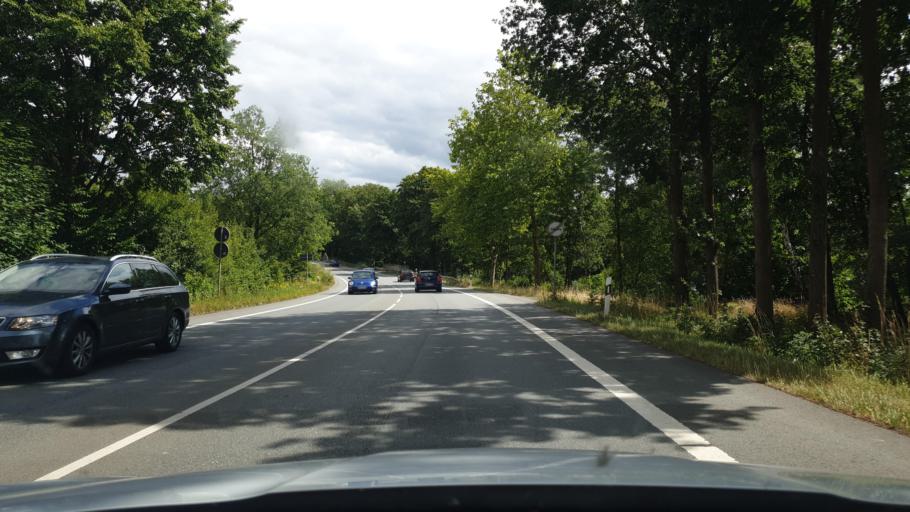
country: DE
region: North Rhine-Westphalia
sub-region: Regierungsbezirk Detmold
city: Lemgo
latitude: 52.0299
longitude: 8.8482
